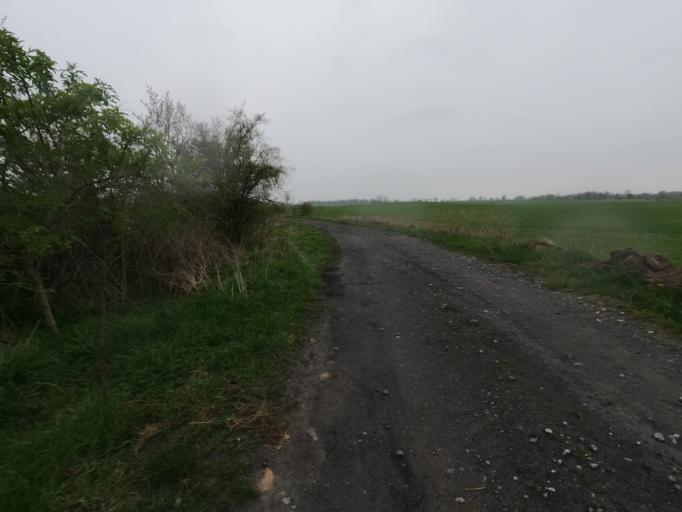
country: PL
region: West Pomeranian Voivodeship
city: Trzcinsko Zdroj
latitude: 52.9218
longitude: 14.7312
